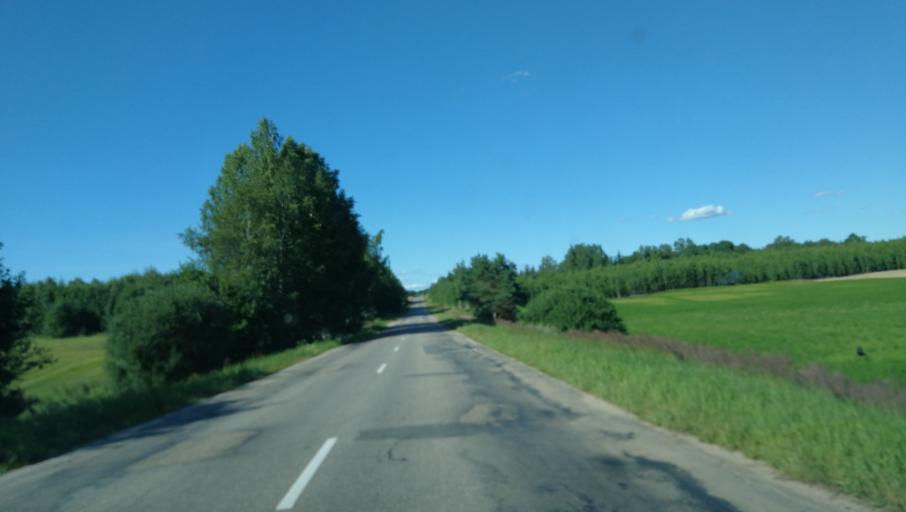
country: LV
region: Madonas Rajons
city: Madona
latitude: 56.9533
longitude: 26.0424
